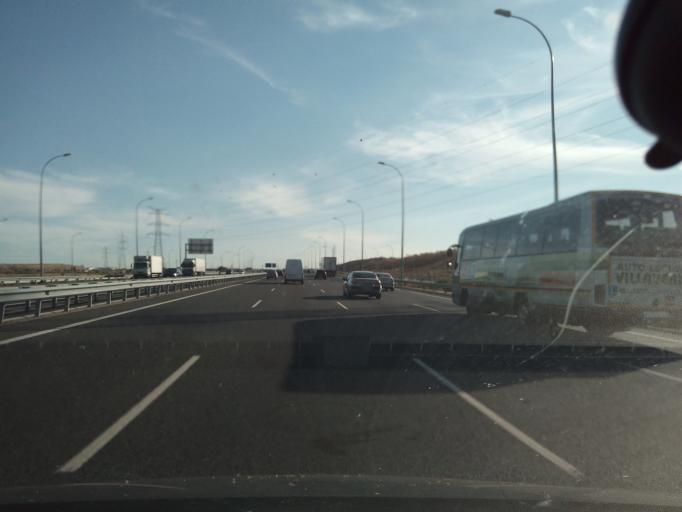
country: ES
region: Madrid
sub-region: Provincia de Madrid
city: Villaverde
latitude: 40.2970
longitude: -3.6689
